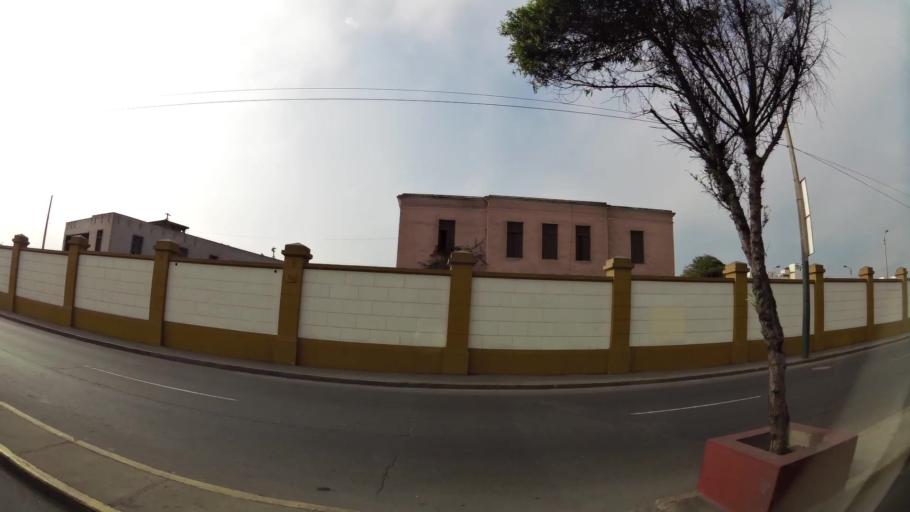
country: PE
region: Lima
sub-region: Lima
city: San Isidro
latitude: -12.0997
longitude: -77.0644
